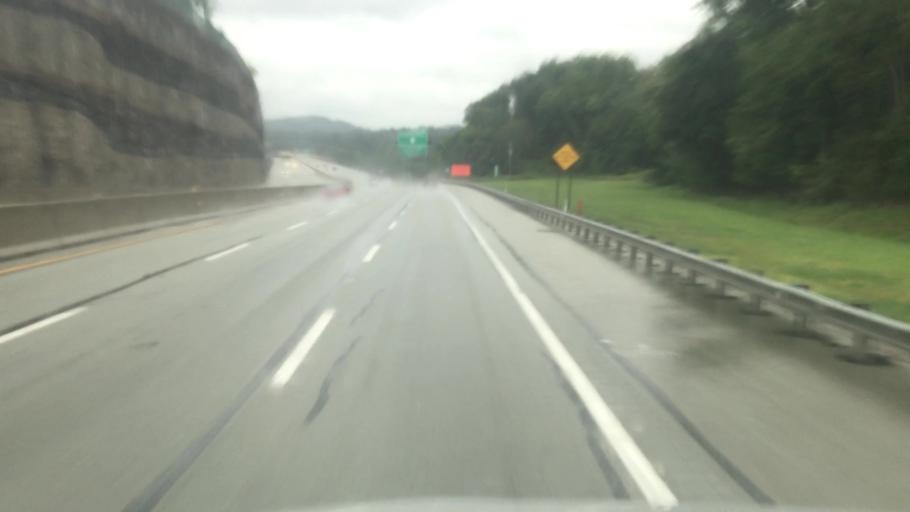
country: US
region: Pennsylvania
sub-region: Allegheny County
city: Oakmont
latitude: 40.5311
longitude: -79.8215
